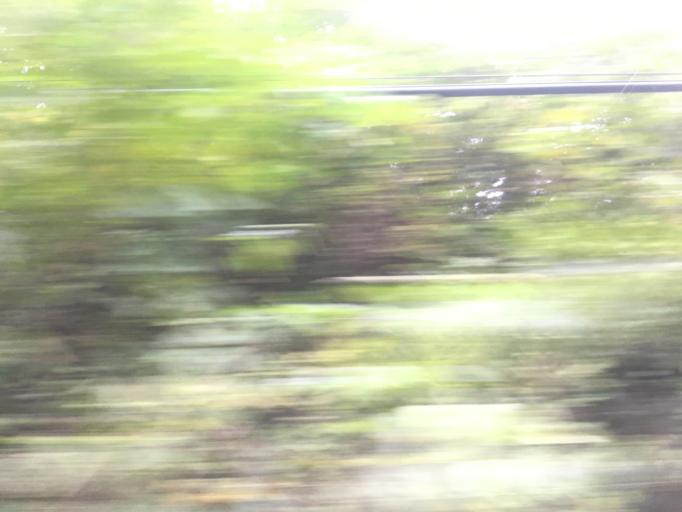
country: JP
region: Saitama
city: Hanno
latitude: 35.8751
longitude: 139.3366
